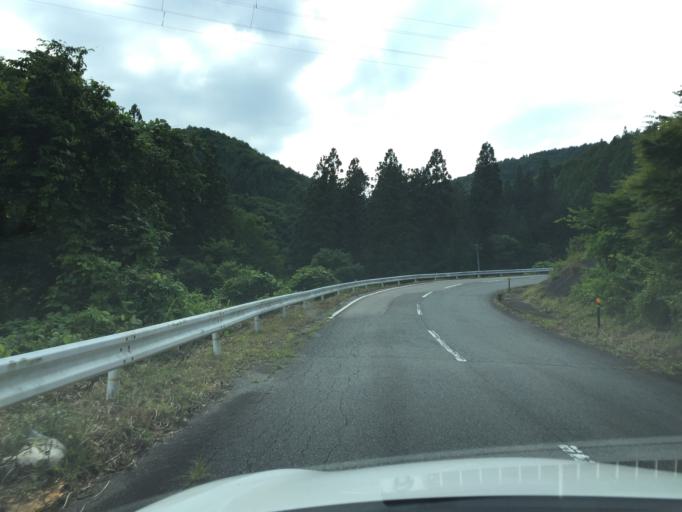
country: JP
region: Fukushima
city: Ishikawa
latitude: 37.1224
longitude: 140.6439
